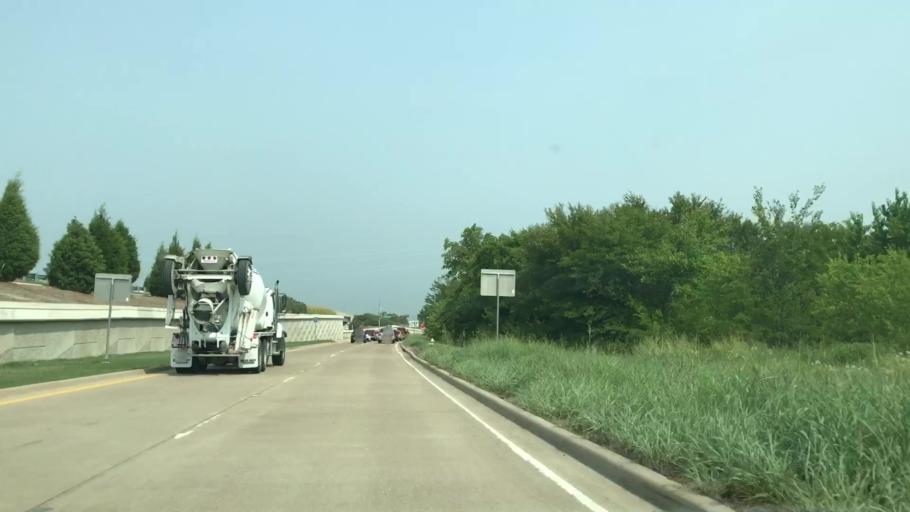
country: US
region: Texas
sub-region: Dallas County
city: Sachse
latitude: 32.9508
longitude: -96.5732
